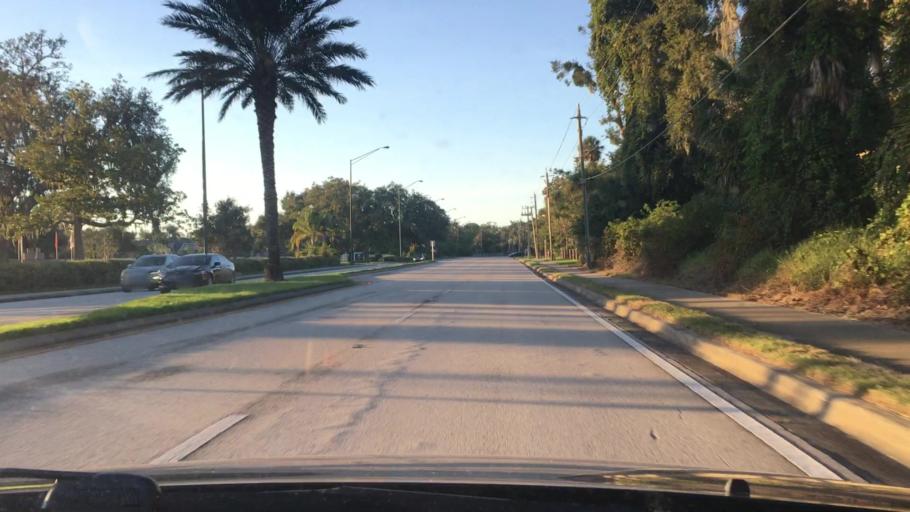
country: US
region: Florida
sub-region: Volusia County
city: Ormond Beach
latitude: 29.2901
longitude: -81.0857
